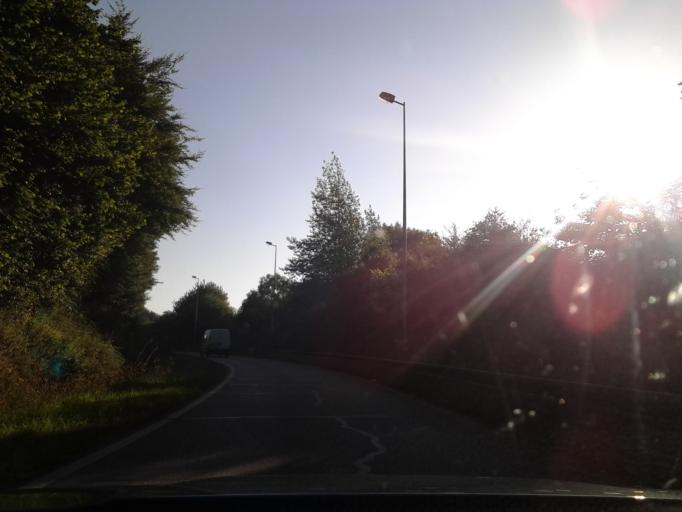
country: FR
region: Lower Normandy
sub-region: Departement de la Manche
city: La Glacerie
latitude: 49.5991
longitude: -1.5958
